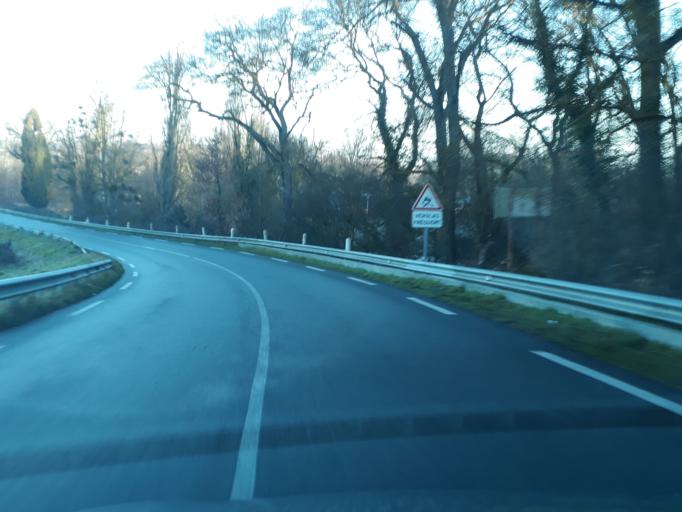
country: FR
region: Midi-Pyrenees
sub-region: Departement de la Haute-Garonne
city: Berat
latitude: 43.3827
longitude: 1.1751
